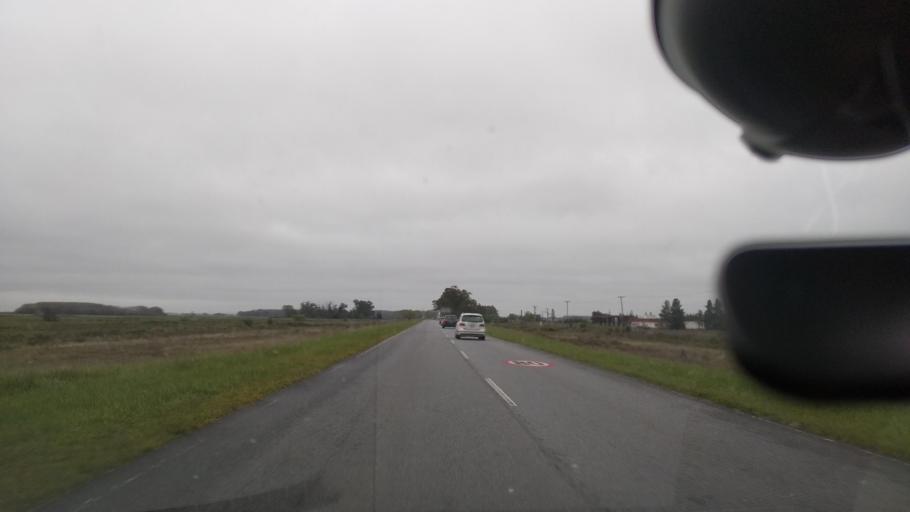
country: AR
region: Buenos Aires
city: Veronica
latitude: -35.3900
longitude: -57.3610
